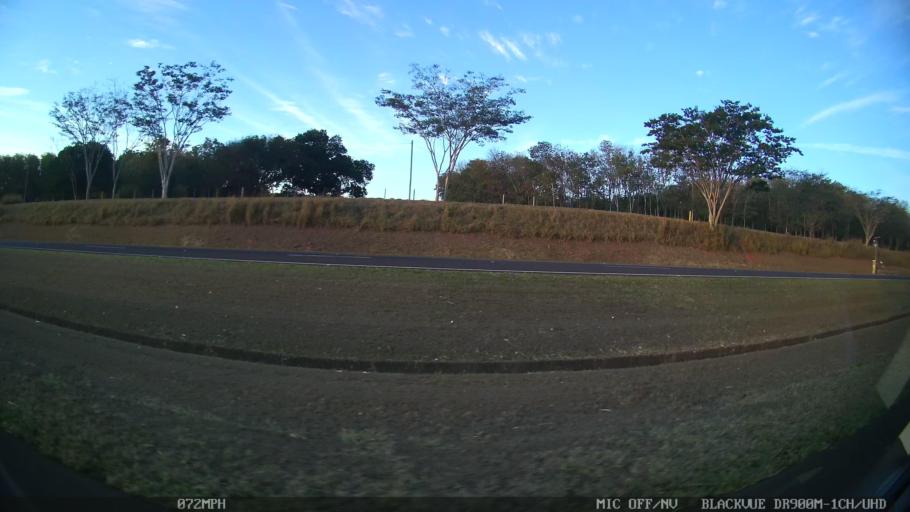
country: BR
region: Sao Paulo
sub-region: Pindorama
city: Pindorama
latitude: -21.2251
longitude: -48.9150
